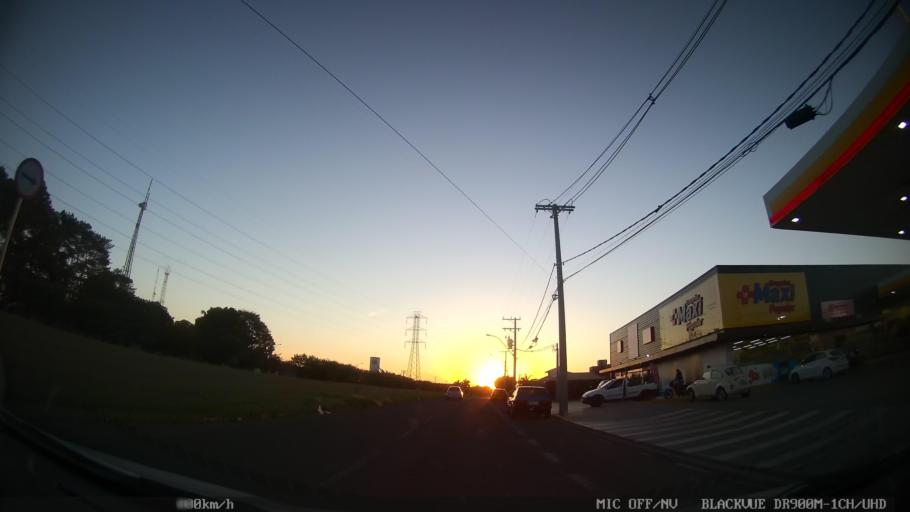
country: BR
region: Sao Paulo
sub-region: Sao Jose Do Rio Preto
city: Sao Jose do Rio Preto
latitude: -20.7999
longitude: -49.3464
